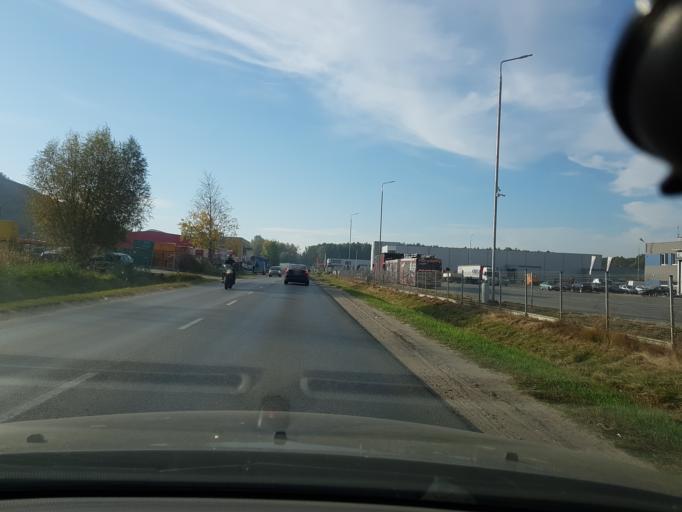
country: PL
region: Masovian Voivodeship
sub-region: Powiat warszawski zachodni
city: Babice
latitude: 52.2785
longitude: 20.8756
